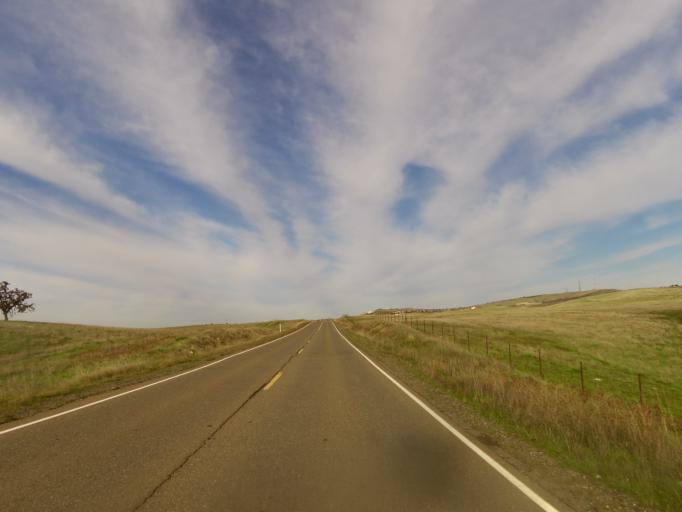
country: US
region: California
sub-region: El Dorado County
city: El Dorado Hills
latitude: 38.6269
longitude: -121.1141
